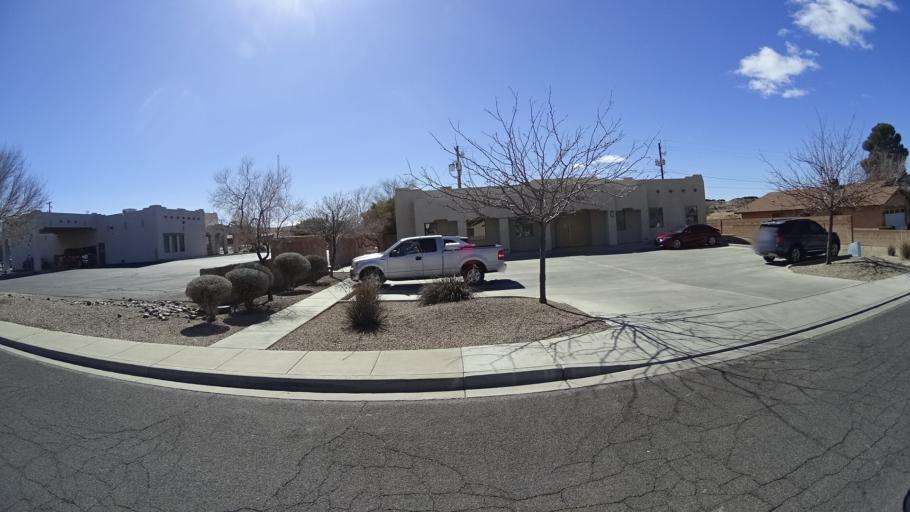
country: US
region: Arizona
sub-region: Mohave County
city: Kingman
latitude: 35.1922
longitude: -114.0210
